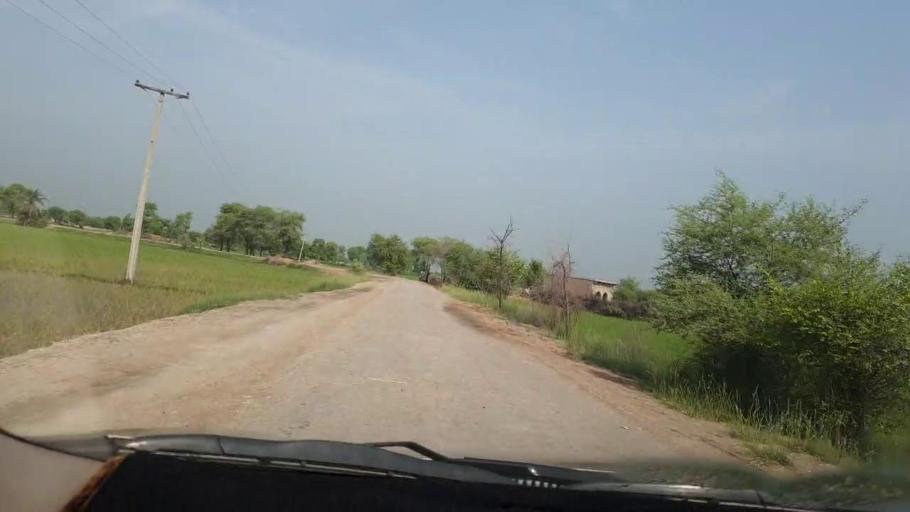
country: PK
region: Sindh
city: Goth Garelo
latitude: 27.4498
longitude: 68.0254
